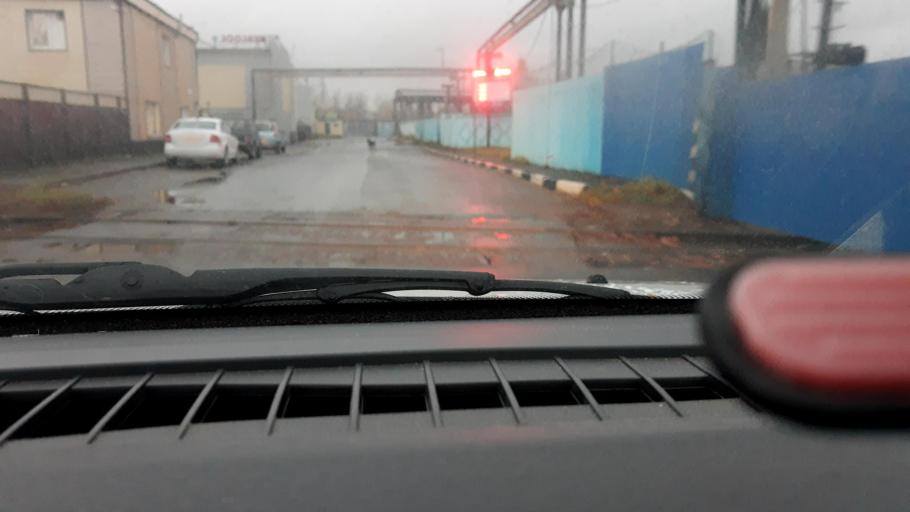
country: RU
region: Nizjnij Novgorod
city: Neklyudovo
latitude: 56.3479
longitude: 43.8896
